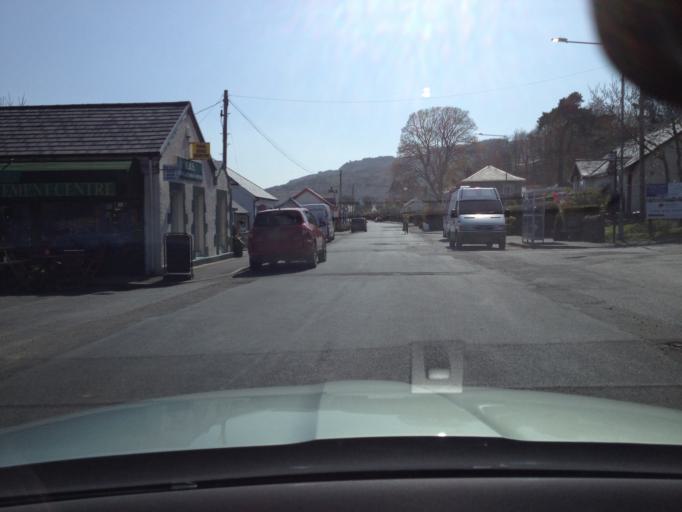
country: GB
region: Scotland
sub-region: North Ayrshire
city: Lamlash
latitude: 55.4906
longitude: -5.0951
